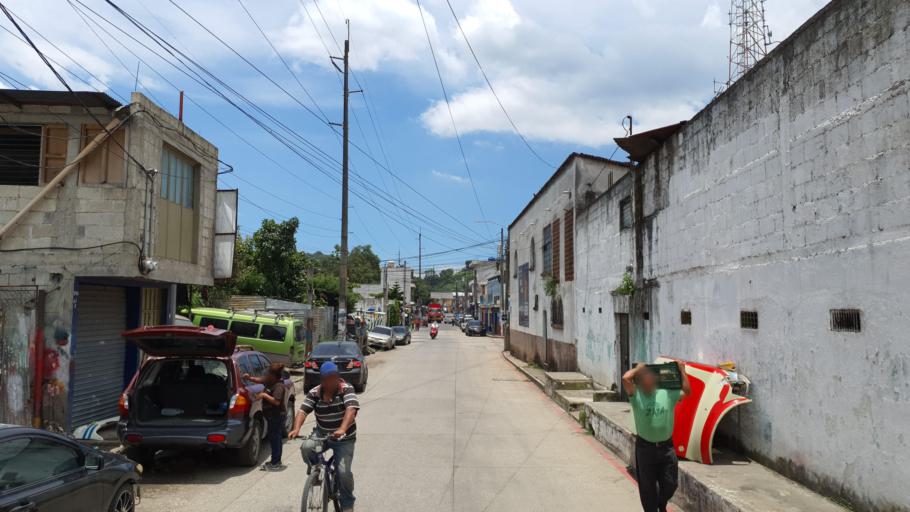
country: GT
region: Guatemala
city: Villa Canales
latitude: 14.4818
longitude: -90.5353
